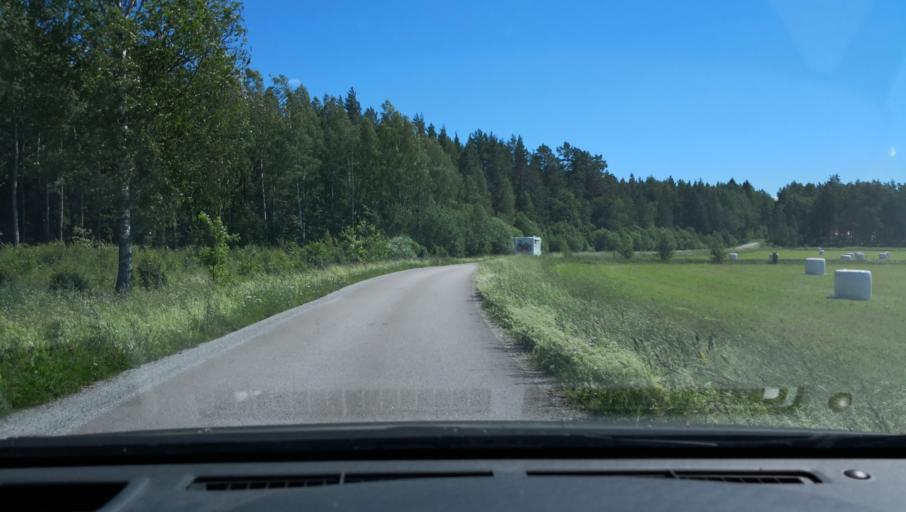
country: SE
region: Vaestmanland
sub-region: Arboga Kommun
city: Tyringe
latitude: 59.3923
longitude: 15.9425
